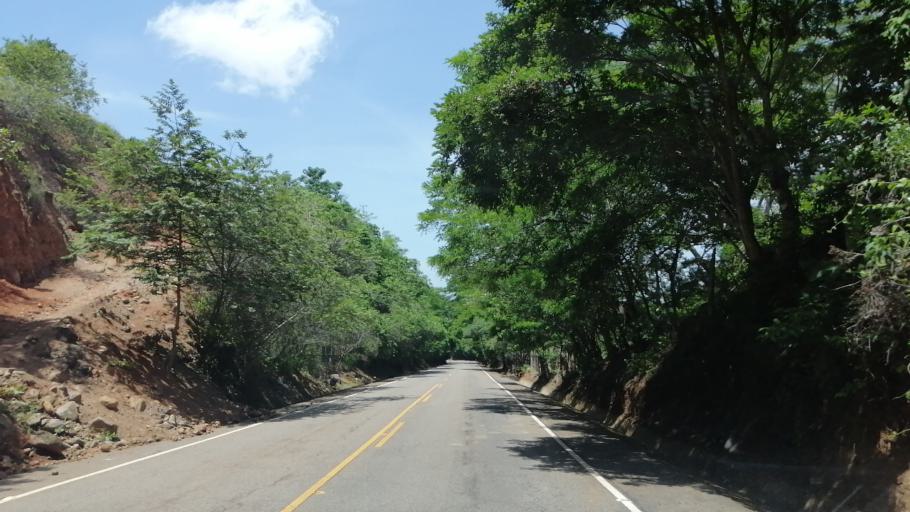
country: SV
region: Chalatenango
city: Nueva Concepcion
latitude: 14.1742
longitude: -89.3148
